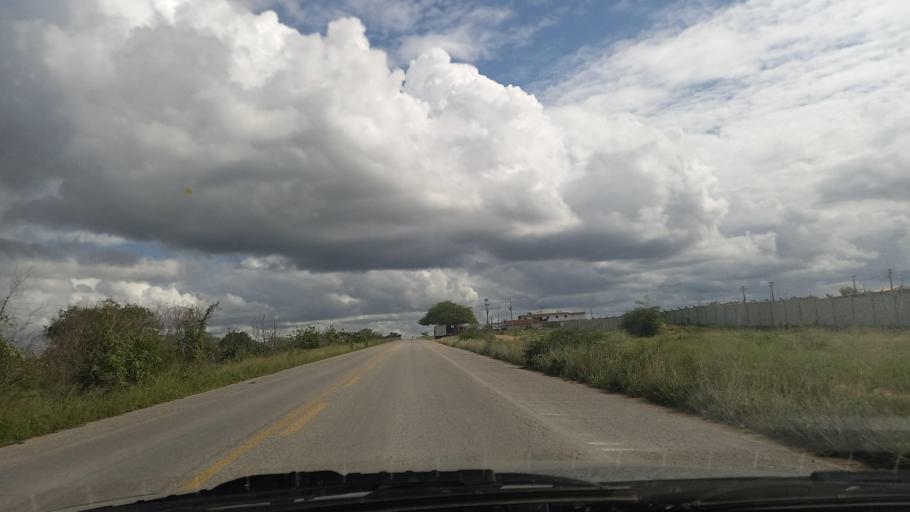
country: BR
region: Pernambuco
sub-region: Cachoeirinha
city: Cachoeirinha
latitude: -8.4958
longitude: -36.2397
